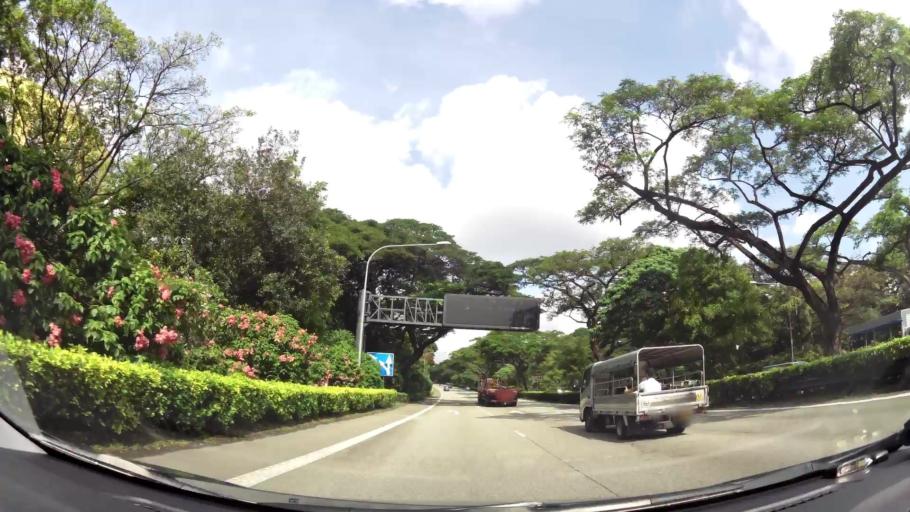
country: SG
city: Singapore
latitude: 1.2753
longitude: 103.8287
